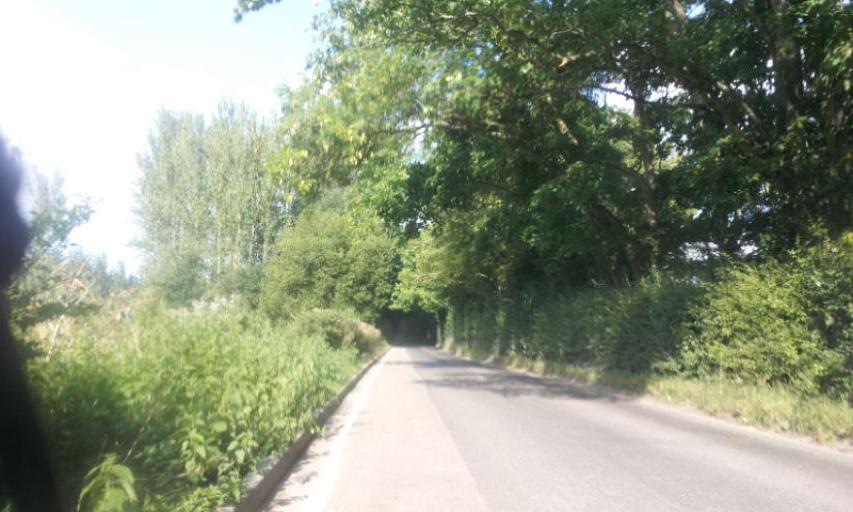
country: GB
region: England
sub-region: Kent
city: Yalding
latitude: 51.2224
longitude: 0.4690
